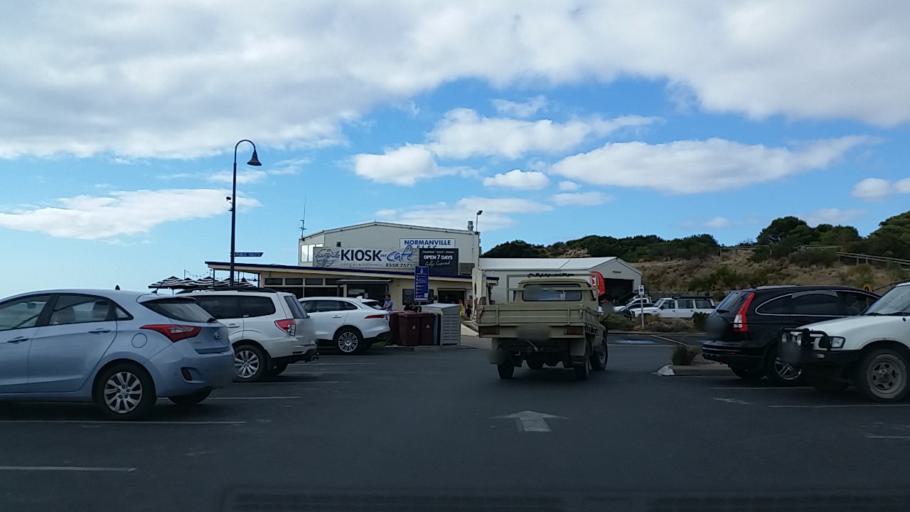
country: AU
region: South Australia
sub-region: Yankalilla
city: Normanville
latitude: -35.4458
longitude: 138.3083
